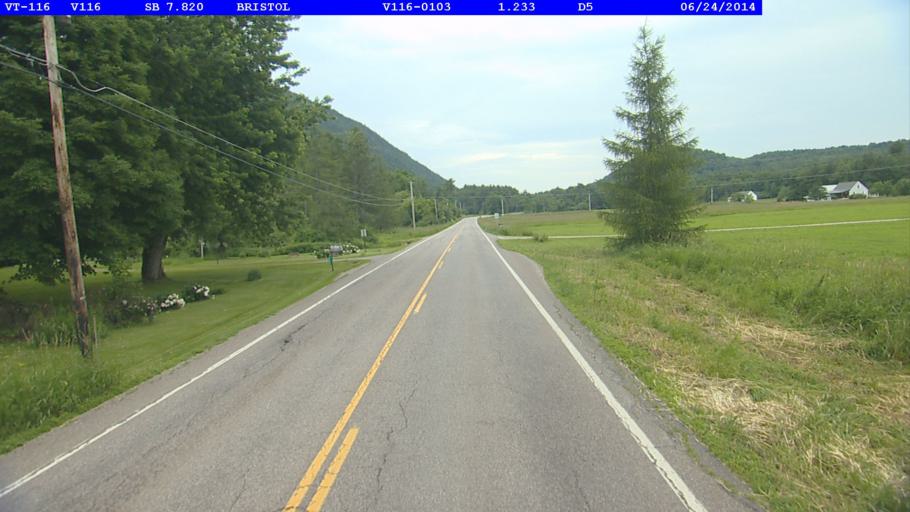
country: US
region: Vermont
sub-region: Addison County
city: Bristol
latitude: 44.0714
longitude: -73.0860
